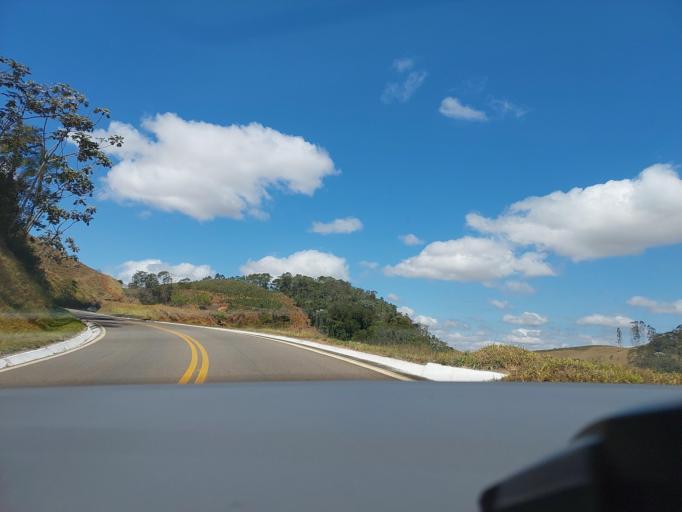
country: BR
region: Minas Gerais
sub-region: Mirai
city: Mirai
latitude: -21.0357
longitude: -42.5370
